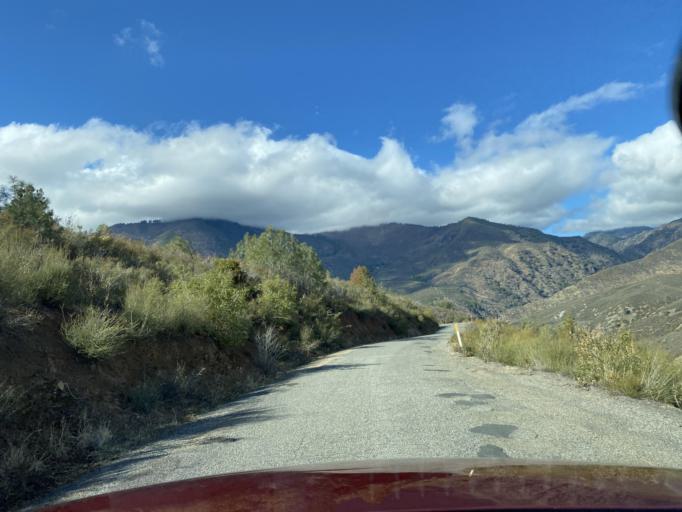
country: US
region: California
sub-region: Lake County
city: Lucerne
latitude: 39.3728
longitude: -122.6440
